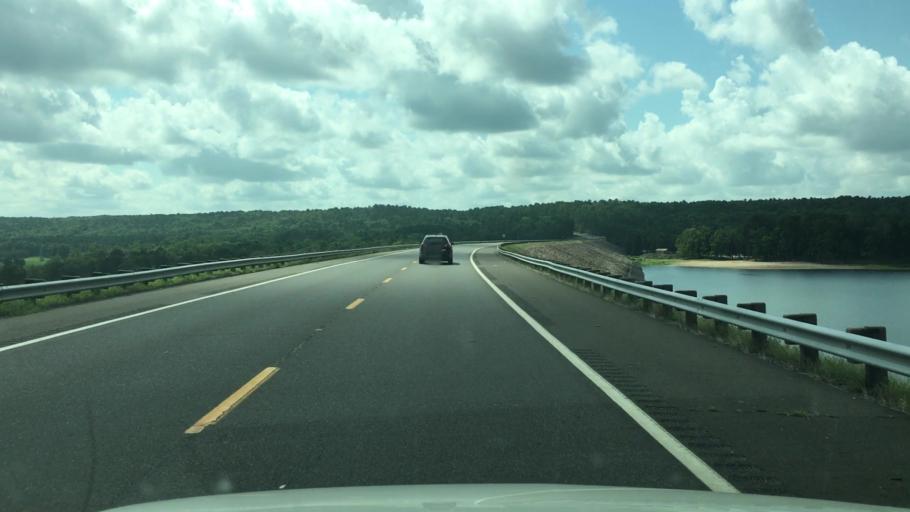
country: US
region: Arkansas
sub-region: Clark County
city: Arkadelphia
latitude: 34.2418
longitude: -93.1051
